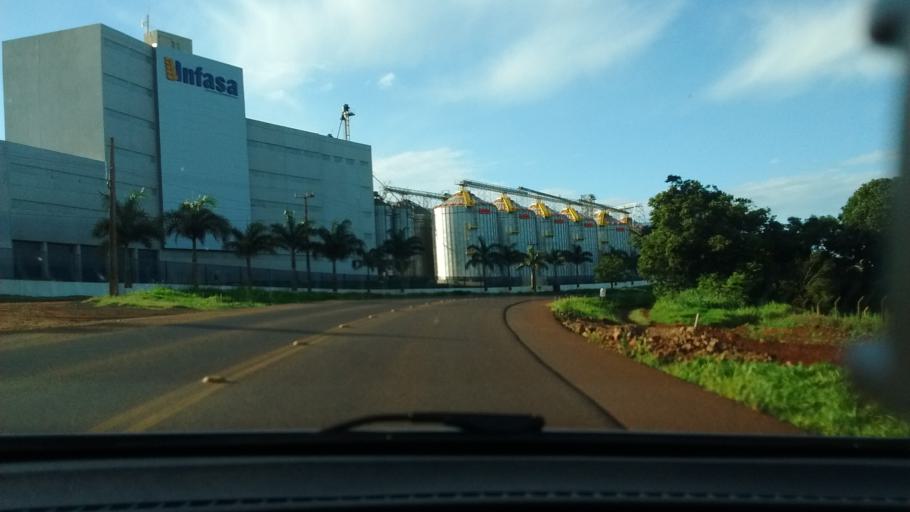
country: BR
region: Parana
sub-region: Cascavel
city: Cascavel
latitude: -25.1357
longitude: -53.5836
